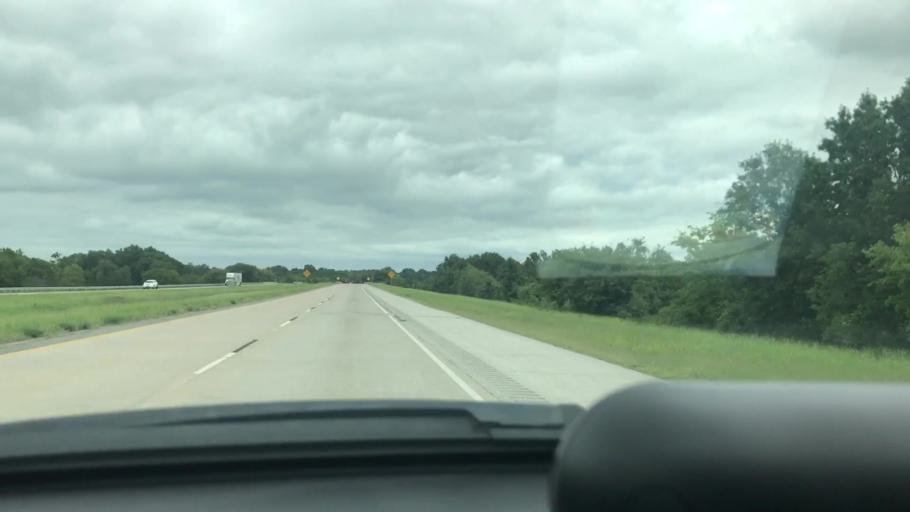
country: US
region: Oklahoma
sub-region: Wagoner County
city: Wagoner
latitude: 35.9047
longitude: -95.4026
